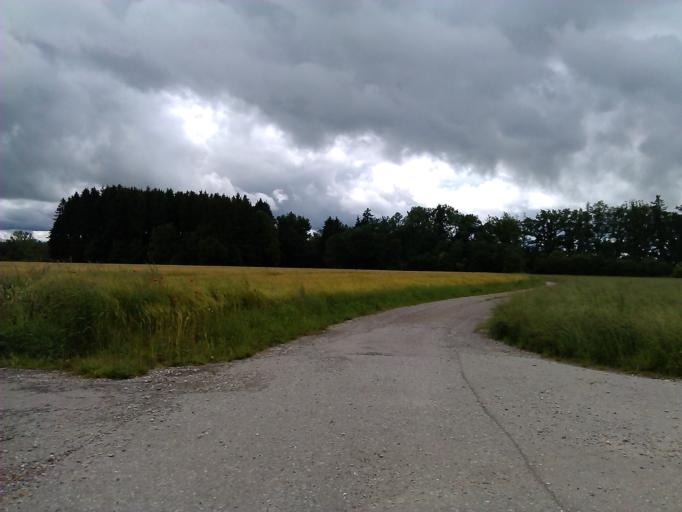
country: DE
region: Bavaria
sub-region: Swabia
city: Pforzen
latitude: 47.9529
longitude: 10.6210
